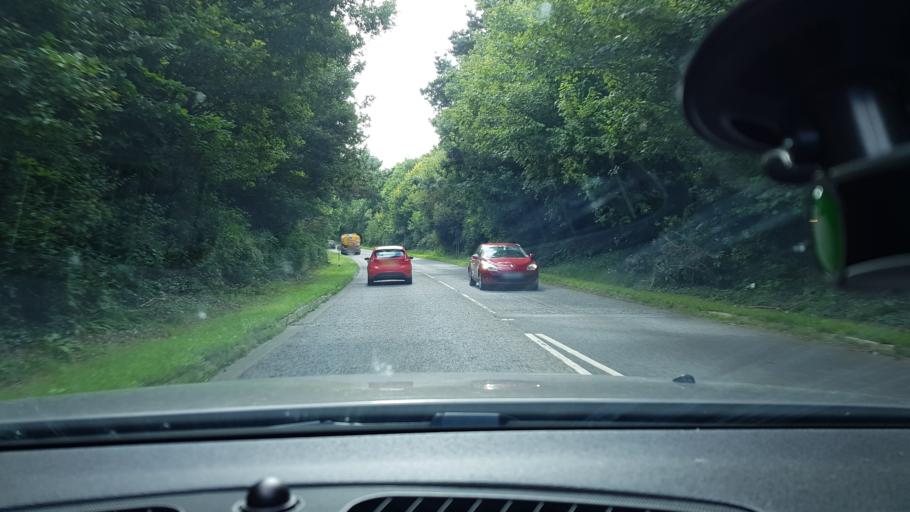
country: GB
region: England
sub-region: Cornwall
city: Penzance
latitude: 50.1174
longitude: -5.5548
